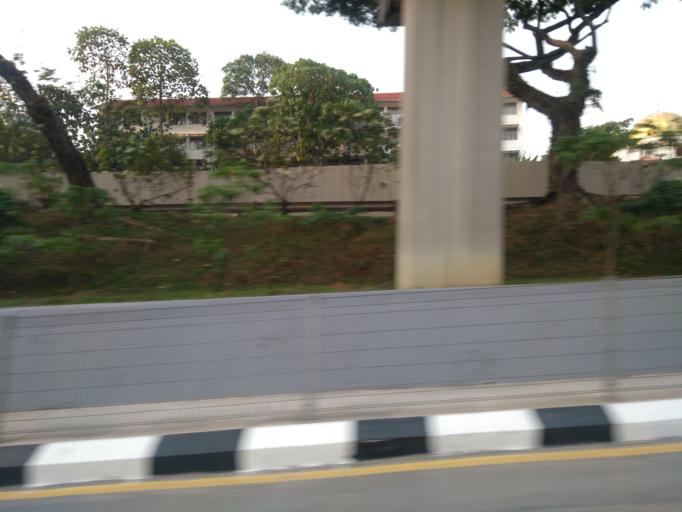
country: MY
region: Kuala Lumpur
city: Kuala Lumpur
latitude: 3.1373
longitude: 101.7016
